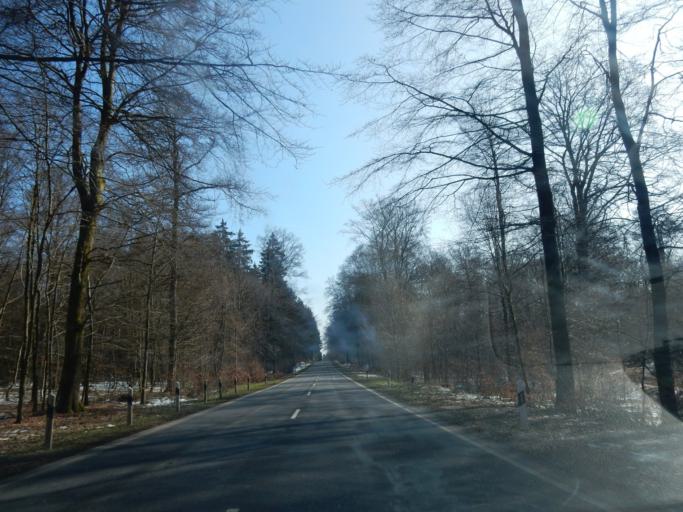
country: LU
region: Diekirch
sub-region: Canton de Redange
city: Rambrouch
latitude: 49.8411
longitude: 5.8027
